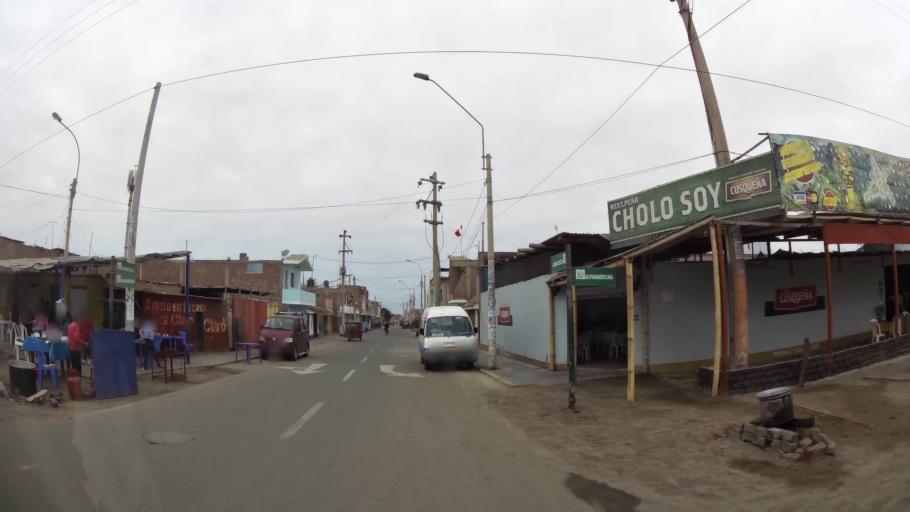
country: PE
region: Lima
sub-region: Provincia de Canete
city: Chilca
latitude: -12.5140
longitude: -76.7355
